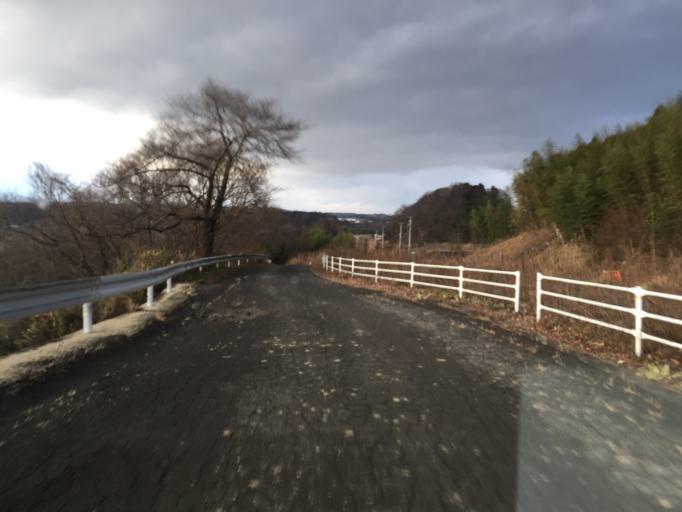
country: JP
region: Fukushima
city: Nihommatsu
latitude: 37.5581
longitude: 140.4410
